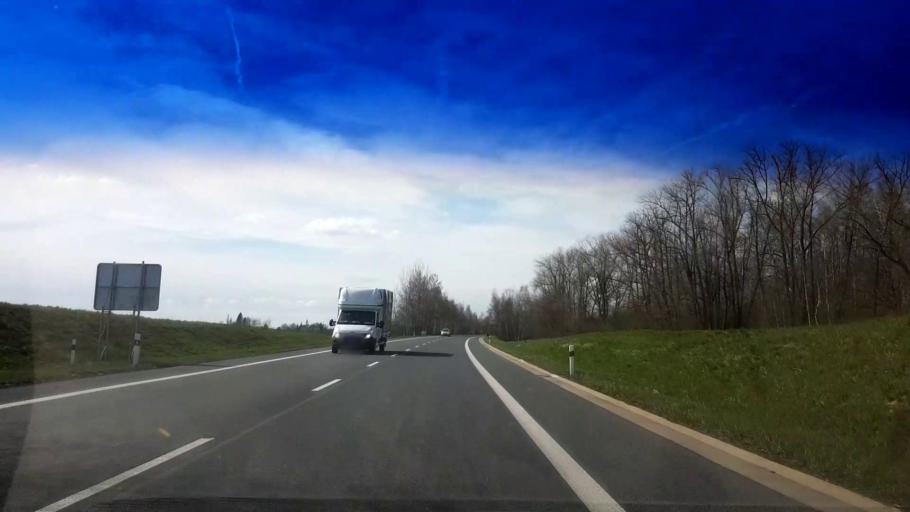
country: CZ
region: Karlovarsky
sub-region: Okres Cheb
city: Frantiskovy Lazne
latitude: 50.0949
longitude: 12.3450
